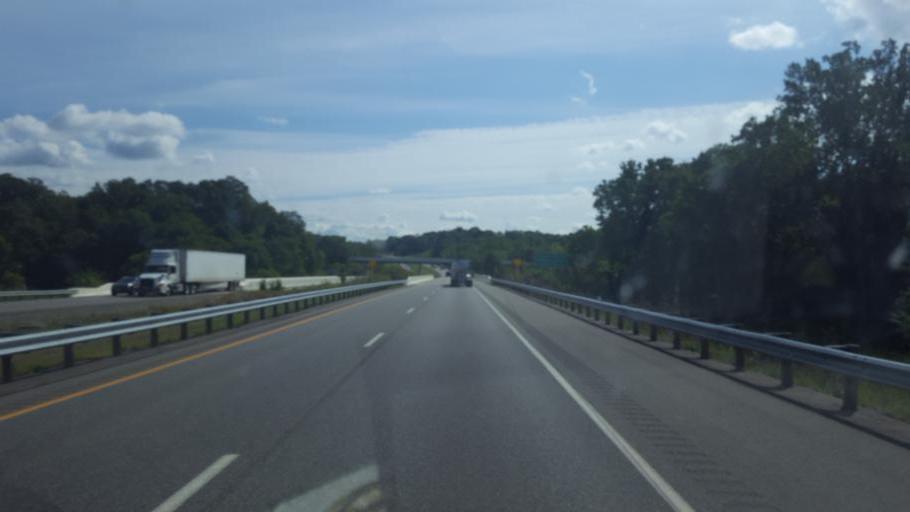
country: US
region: Ohio
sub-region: Summit County
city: Reminderville
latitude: 41.3883
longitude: -81.3900
